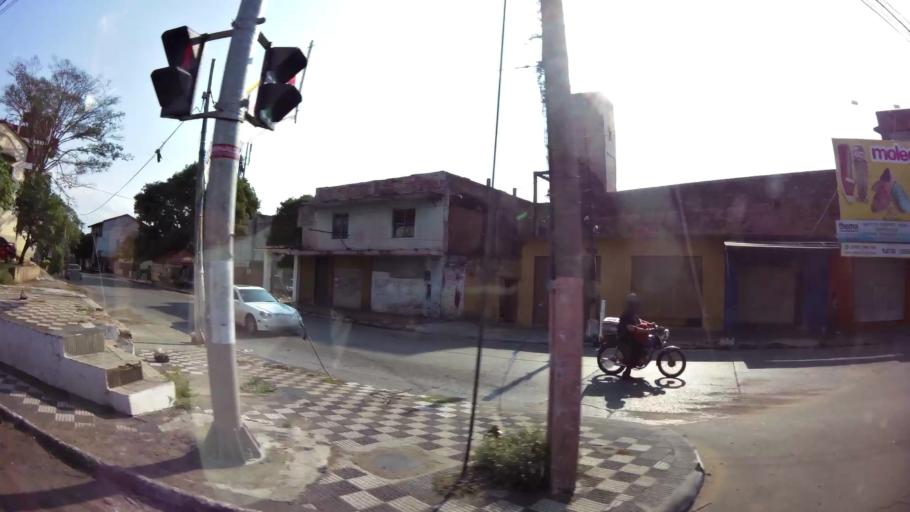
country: PY
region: Asuncion
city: Asuncion
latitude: -25.3057
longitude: -57.6194
